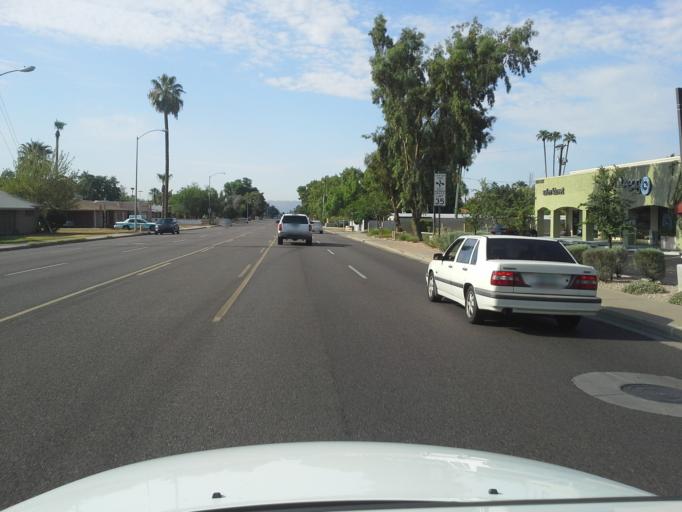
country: US
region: Arizona
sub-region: Maricopa County
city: Phoenix
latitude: 33.5228
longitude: -112.0476
